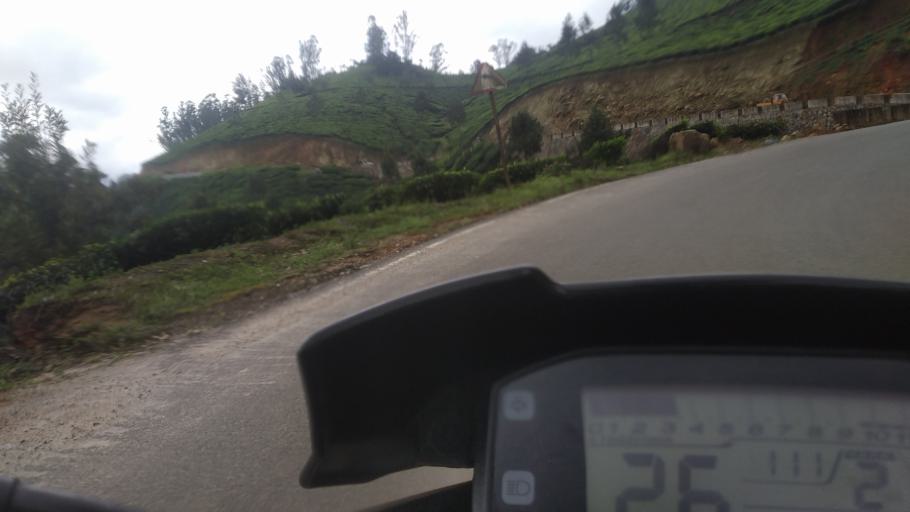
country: IN
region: Kerala
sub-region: Idukki
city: Munnar
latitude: 10.0821
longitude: 77.0752
